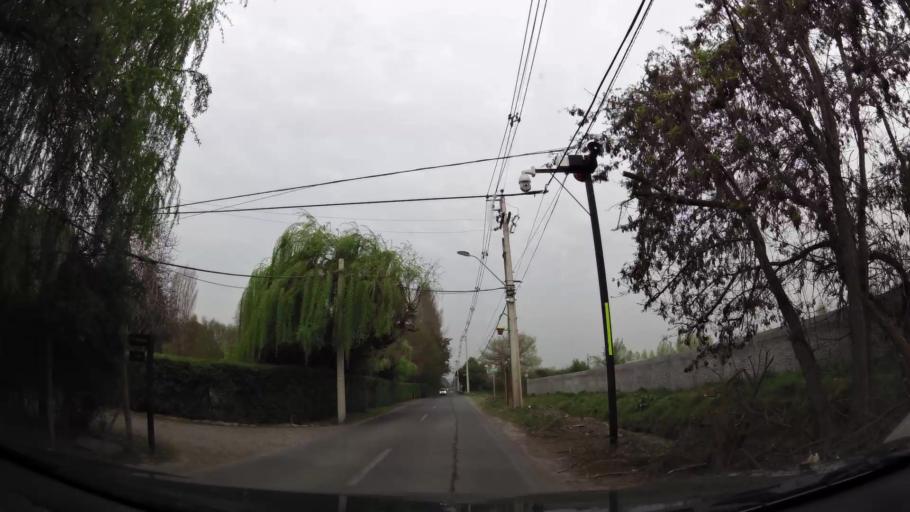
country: CL
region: Santiago Metropolitan
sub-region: Provincia de Chacabuco
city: Chicureo Abajo
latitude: -33.2698
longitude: -70.7126
